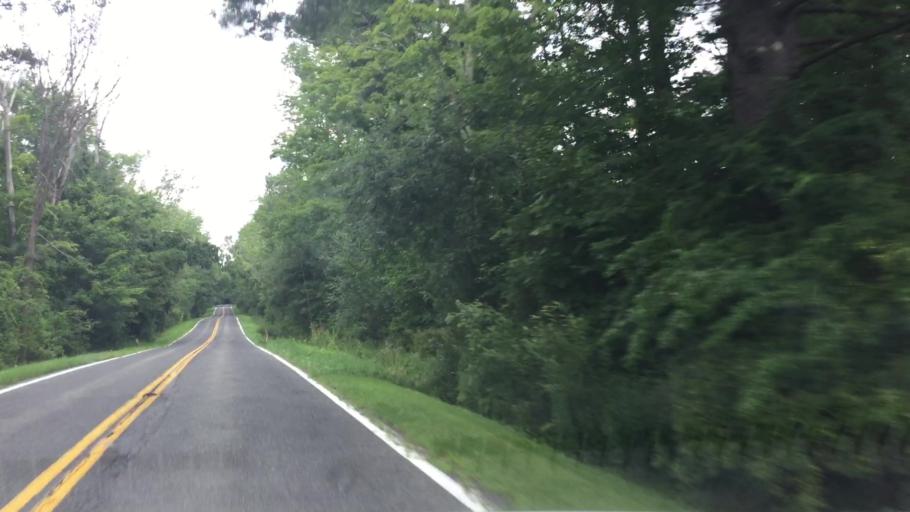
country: US
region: Massachusetts
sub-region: Berkshire County
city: Housatonic
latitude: 42.2774
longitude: -73.4085
